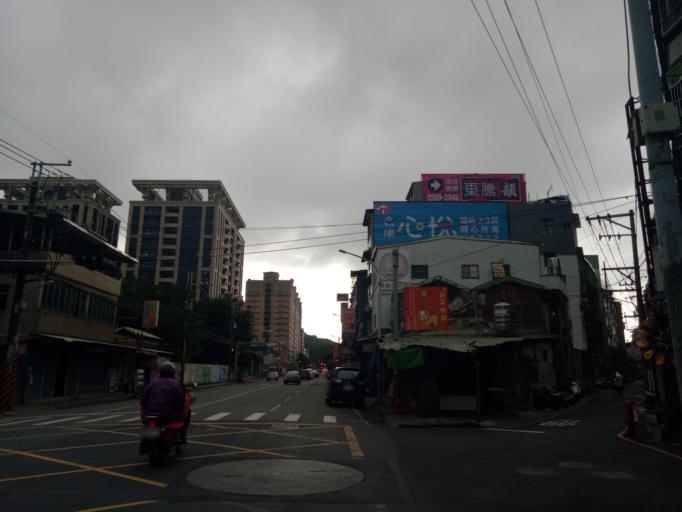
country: TW
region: Taipei
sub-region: Taipei
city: Banqiao
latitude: 24.9560
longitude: 121.4139
